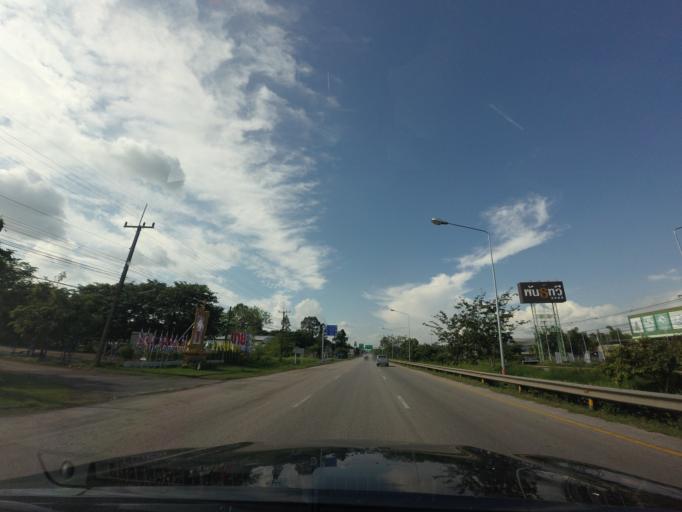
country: TH
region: Nong Khai
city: Sa Khrai
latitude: 17.7636
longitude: 102.7692
